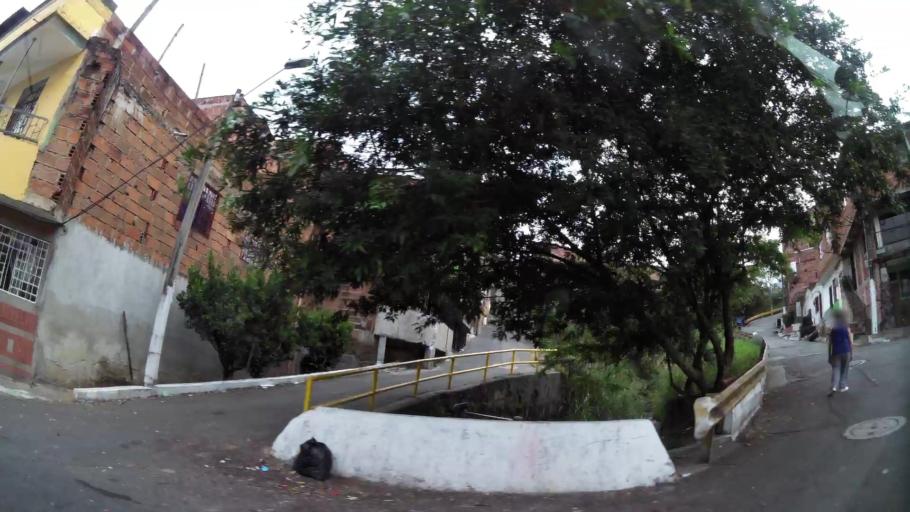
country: CO
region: Antioquia
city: Medellin
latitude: 6.2892
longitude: -75.5553
